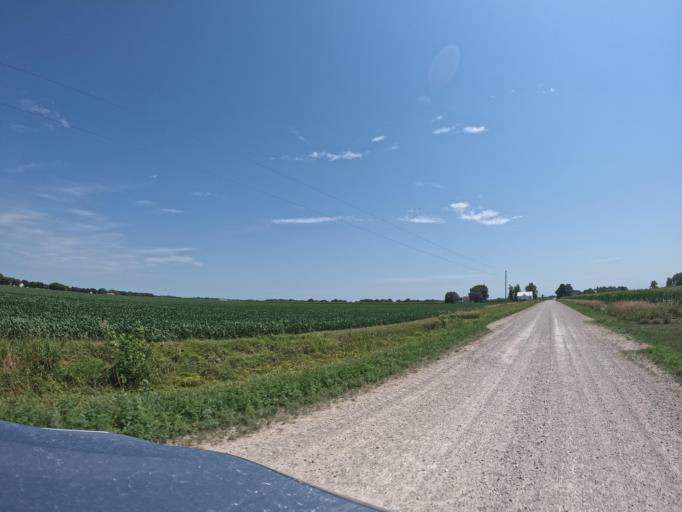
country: US
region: Iowa
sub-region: Henry County
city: Mount Pleasant
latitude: 40.9037
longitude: -91.6316
